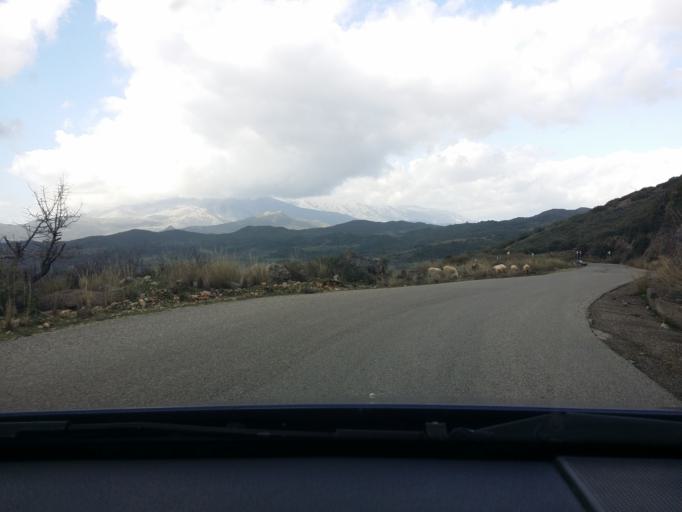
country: GR
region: West Greece
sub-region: Nomos Aitolias kai Akarnanias
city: Fitiai
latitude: 38.6928
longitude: 21.1783
